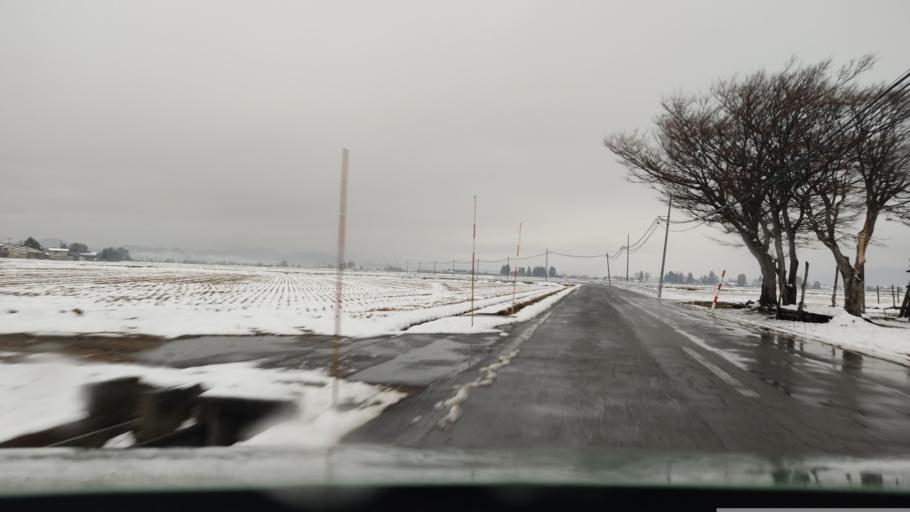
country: JP
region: Akita
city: Omagari
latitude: 39.4726
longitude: 140.5286
